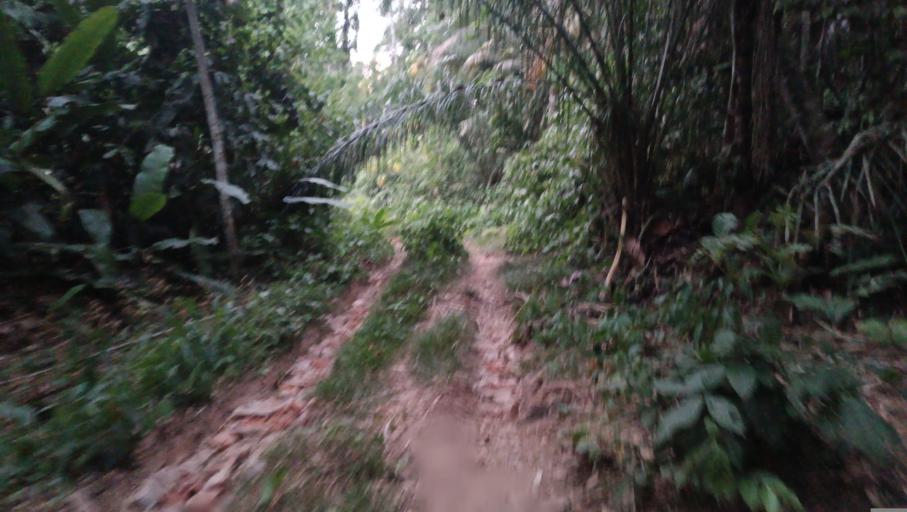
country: BO
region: La Paz
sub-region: Provincia Larecaja
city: Guanay
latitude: -15.5683
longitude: -67.3269
